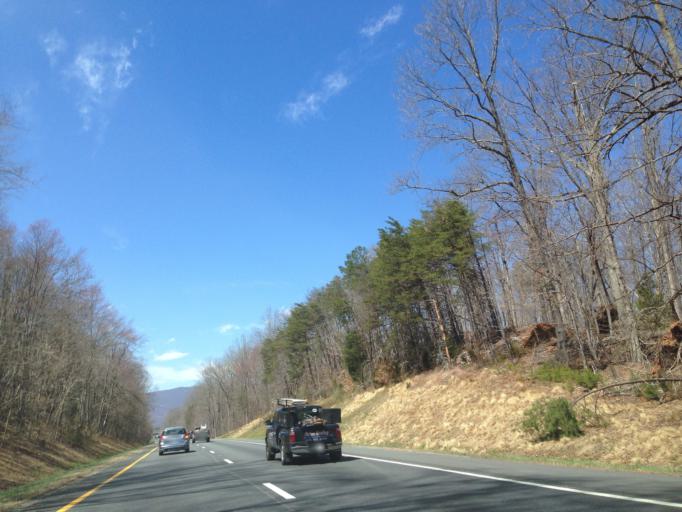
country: US
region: Virginia
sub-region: Albemarle County
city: Crozet
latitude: 38.0346
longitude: -78.6917
